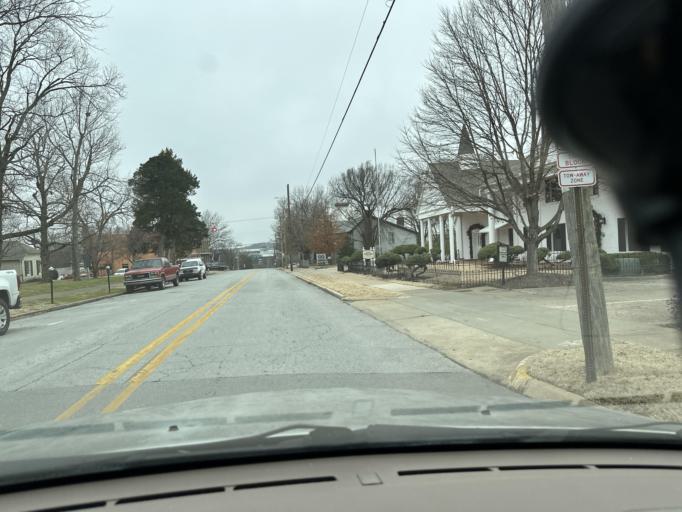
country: US
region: Arkansas
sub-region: Washington County
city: Fayetteville
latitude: 36.0627
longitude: -94.1620
